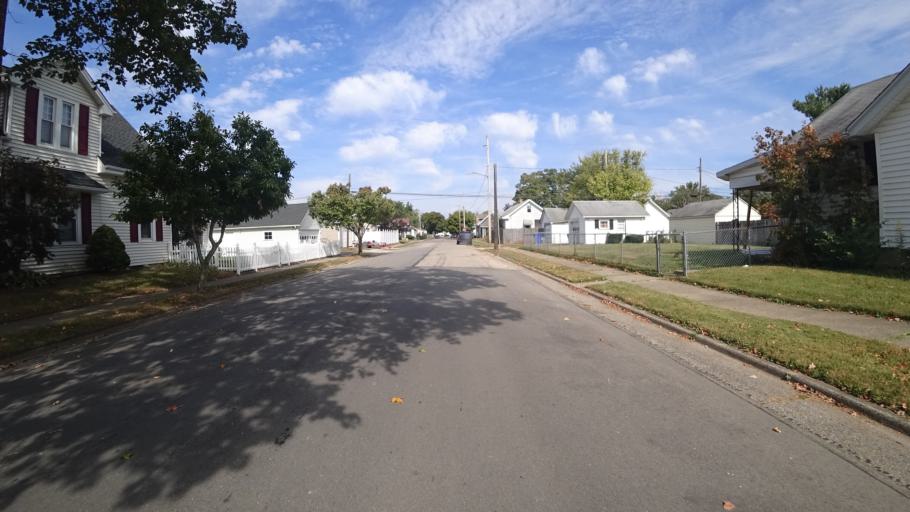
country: US
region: Ohio
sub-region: Butler County
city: Fairfield
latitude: 39.3630
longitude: -84.5545
